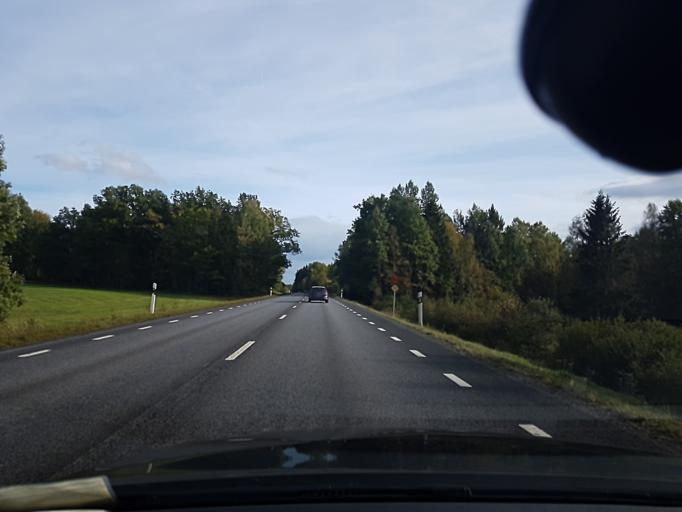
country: SE
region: Joenkoeping
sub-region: Varnamo Kommun
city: Bor
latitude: 57.1429
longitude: 14.1029
